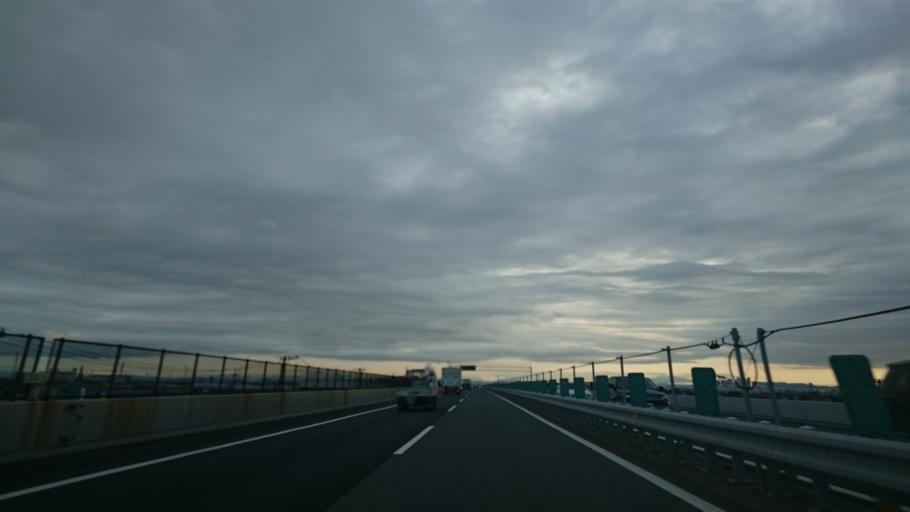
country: JP
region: Aichi
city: Kanie
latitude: 35.1364
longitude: 136.7613
